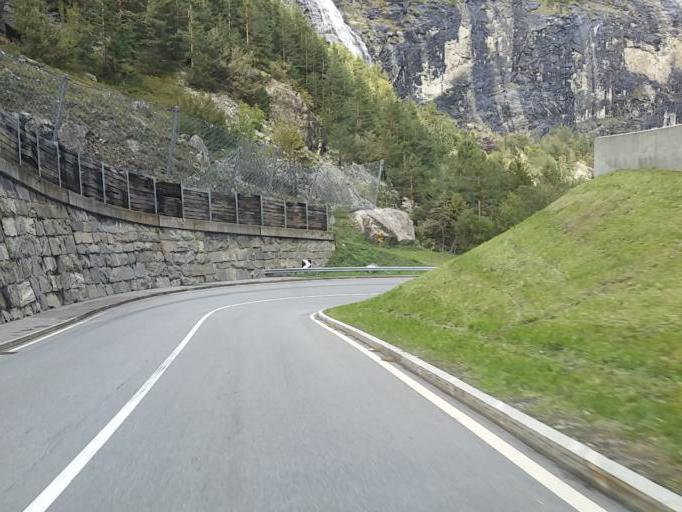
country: IT
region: Piedmont
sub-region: Provincia Verbano-Cusio-Ossola
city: Trasquera
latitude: 46.1988
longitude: 8.1269
